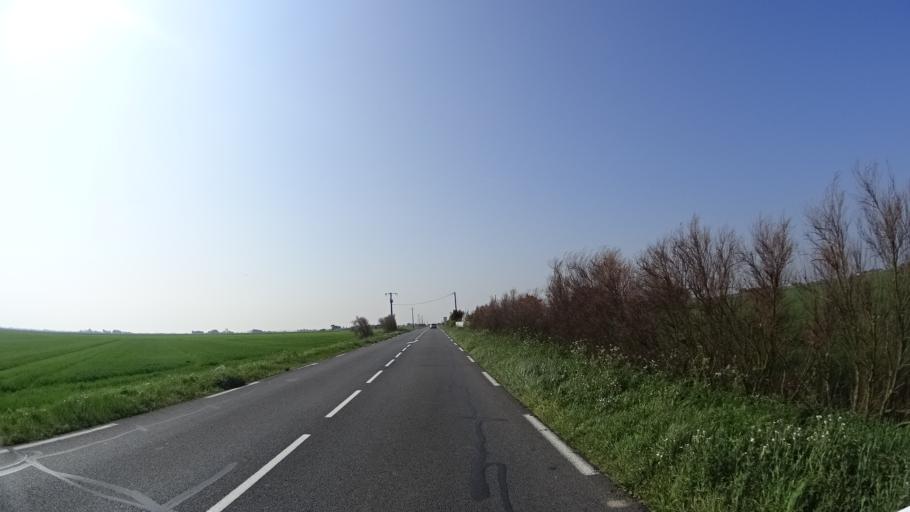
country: FR
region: Pays de la Loire
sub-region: Departement de la Loire-Atlantique
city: Bourgneuf-en-Retz
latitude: 47.0101
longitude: -1.9615
